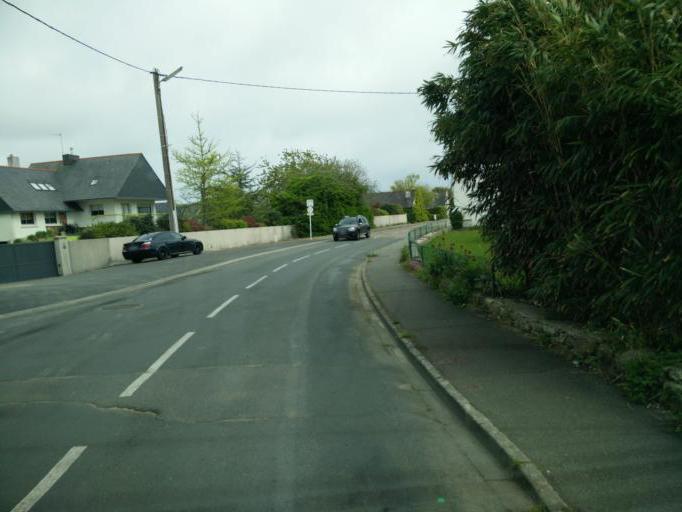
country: FR
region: Brittany
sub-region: Departement du Finistere
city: Loctudy
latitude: 47.8123
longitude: -4.1779
